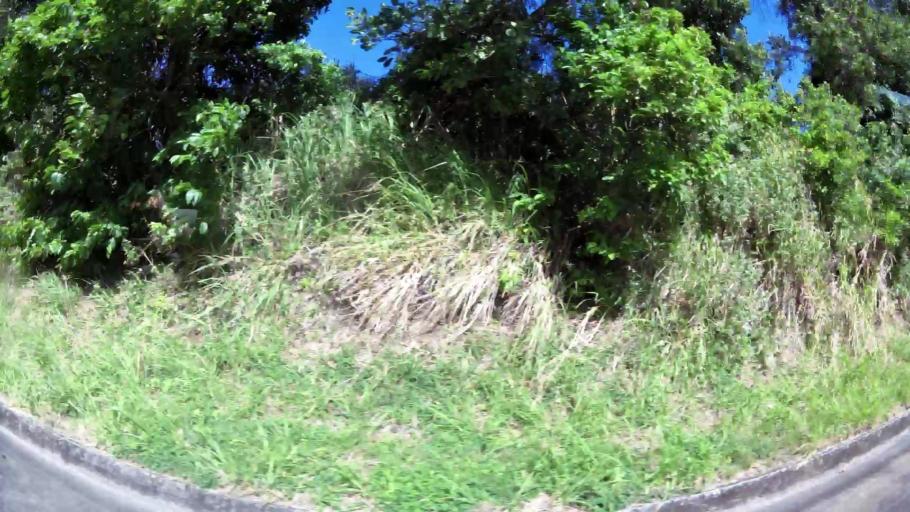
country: MQ
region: Martinique
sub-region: Martinique
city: Le Lorrain
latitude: 14.8357
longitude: -61.0696
